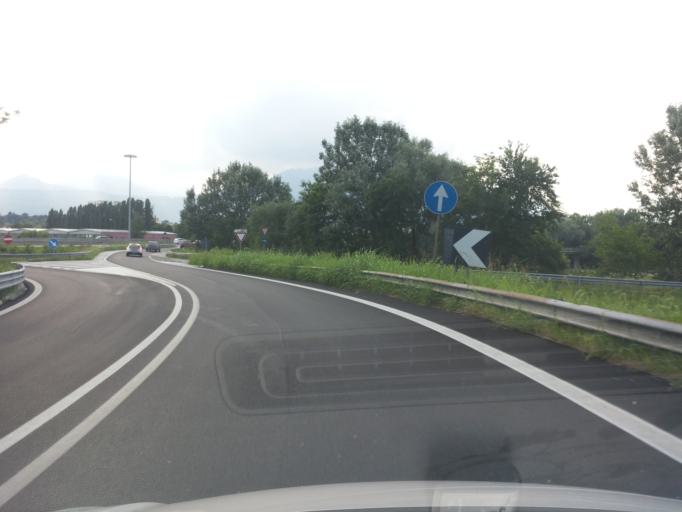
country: IT
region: Piedmont
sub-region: Provincia di Torino
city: Ivrea
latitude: 45.4585
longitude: 7.8872
